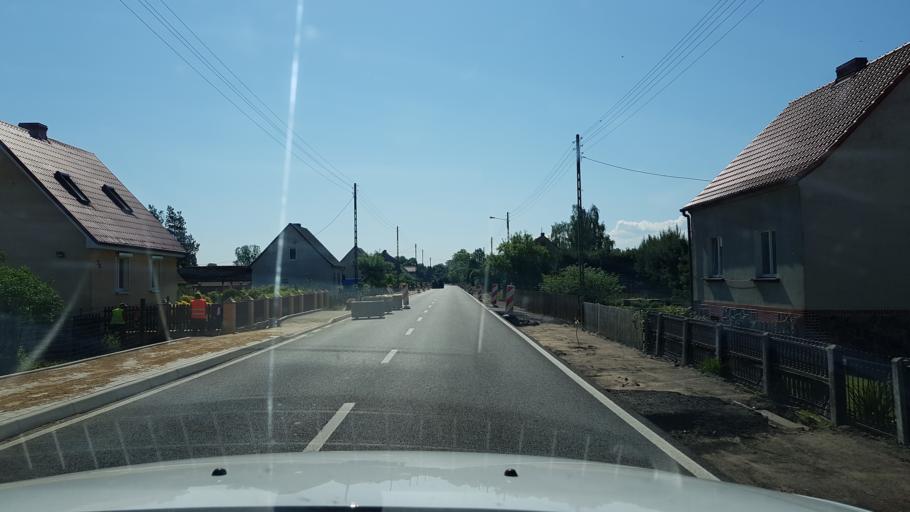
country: PL
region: West Pomeranian Voivodeship
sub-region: Powiat mysliborski
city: Boleszkowice
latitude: 52.6900
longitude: 14.6293
